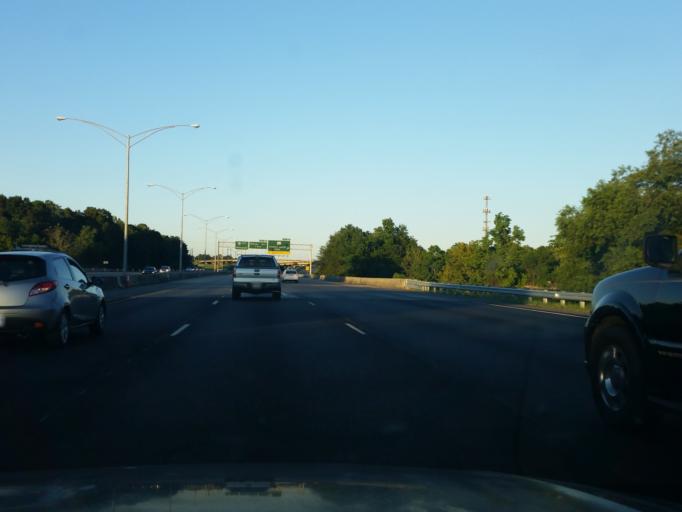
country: US
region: Alabama
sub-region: Mobile County
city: Mobile
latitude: 30.6360
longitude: -88.0969
